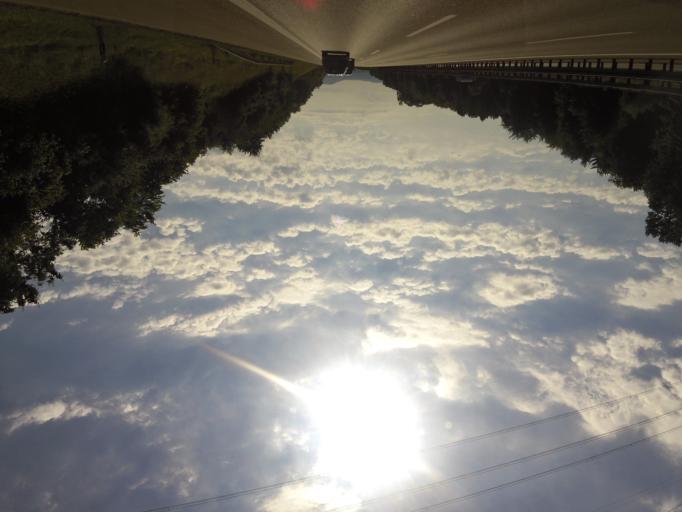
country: DE
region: Baden-Wuerttemberg
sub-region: Regierungsbezirk Stuttgart
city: Wendlingen am Neckar
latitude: 48.6532
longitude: 9.3966
